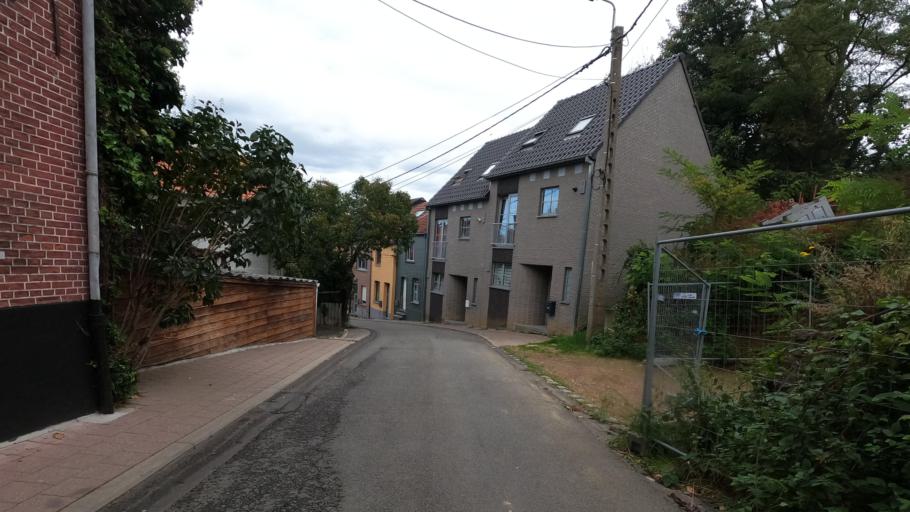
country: BE
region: Flanders
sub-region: Provincie Vlaams-Brabant
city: Aarschot
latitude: 50.9830
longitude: 4.8344
